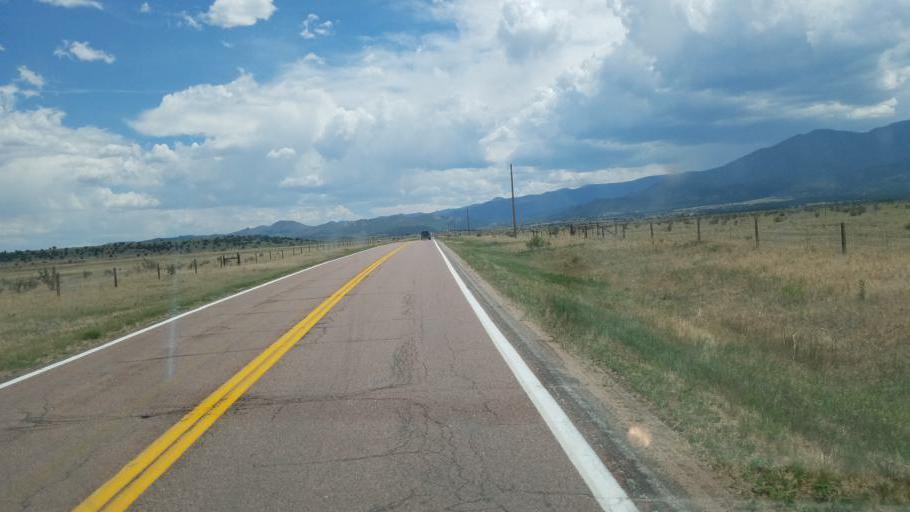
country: US
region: Colorado
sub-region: Fremont County
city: Florence
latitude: 38.2913
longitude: -105.0875
